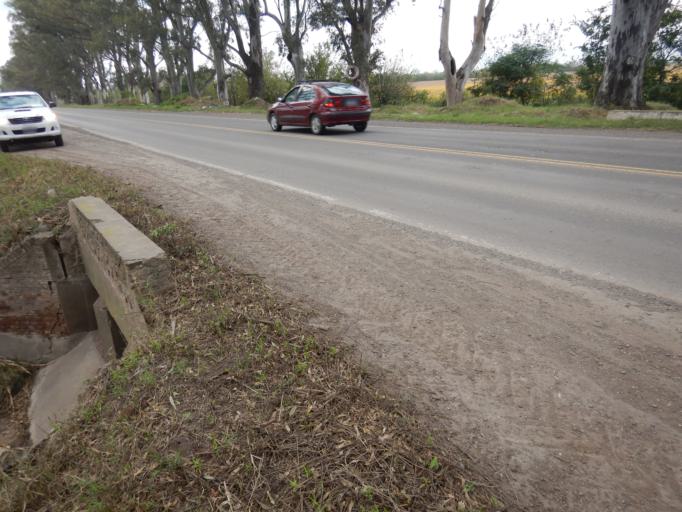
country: AR
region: Santa Fe
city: Roldan
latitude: -32.9024
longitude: -60.9260
